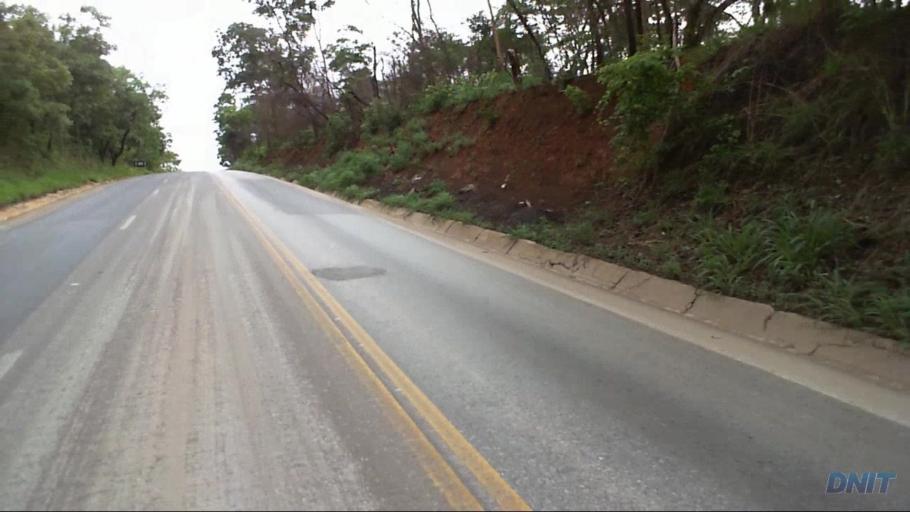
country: BR
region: Goias
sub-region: Uruacu
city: Uruacu
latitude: -14.5998
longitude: -49.1649
